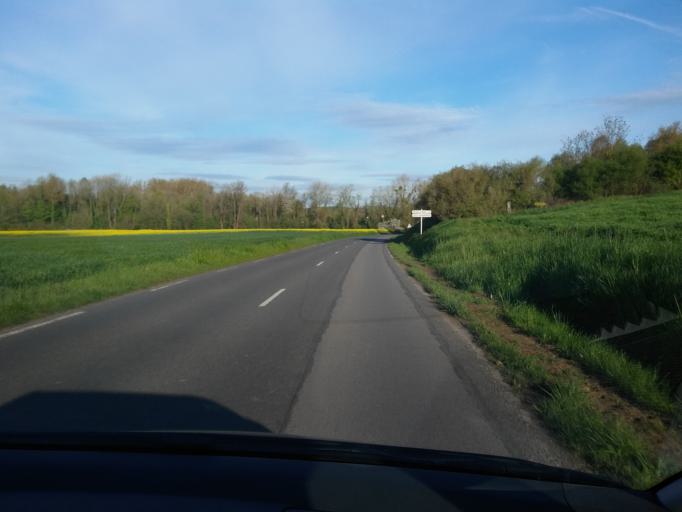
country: FR
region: Picardie
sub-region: Departement de l'Oise
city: Longueil-Sainte-Marie
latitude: 49.3486
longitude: 2.7266
